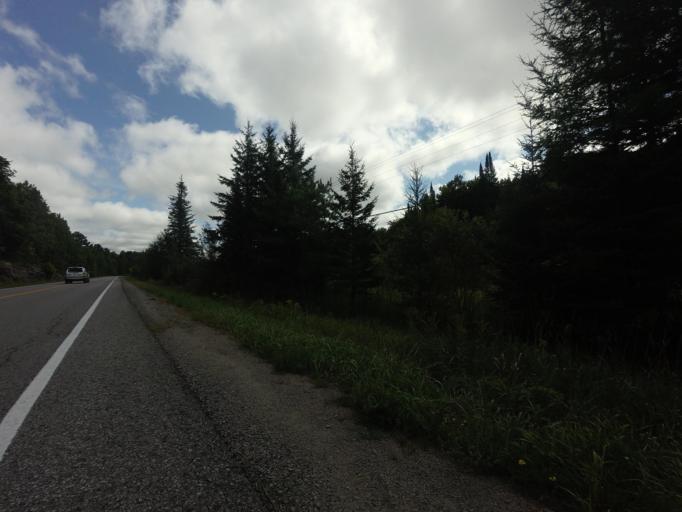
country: CA
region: Ontario
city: Omemee
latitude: 44.8012
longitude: -78.6292
